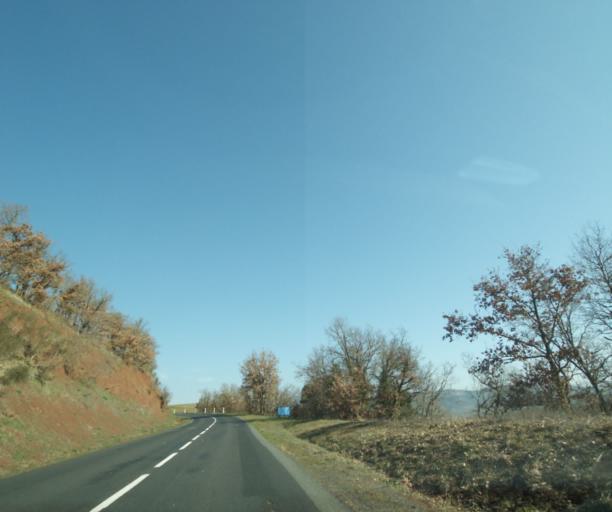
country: FR
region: Midi-Pyrenees
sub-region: Departement de l'Aveyron
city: Camares
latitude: 43.8717
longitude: 2.8211
